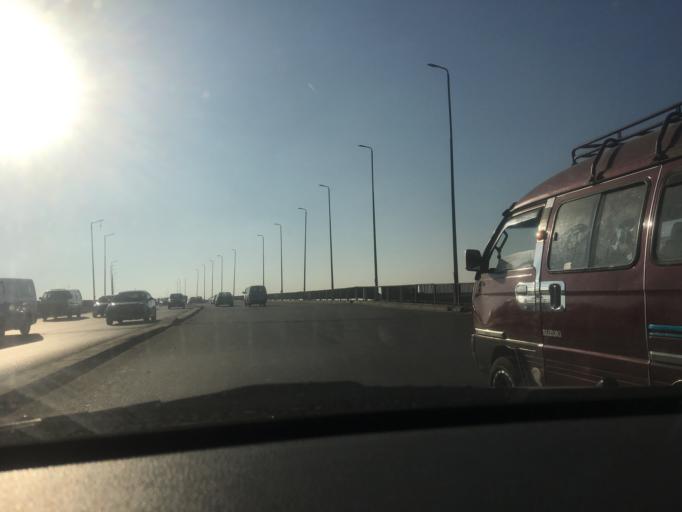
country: EG
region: Muhafazat al Qahirah
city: Cairo
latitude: 30.0104
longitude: 31.2681
